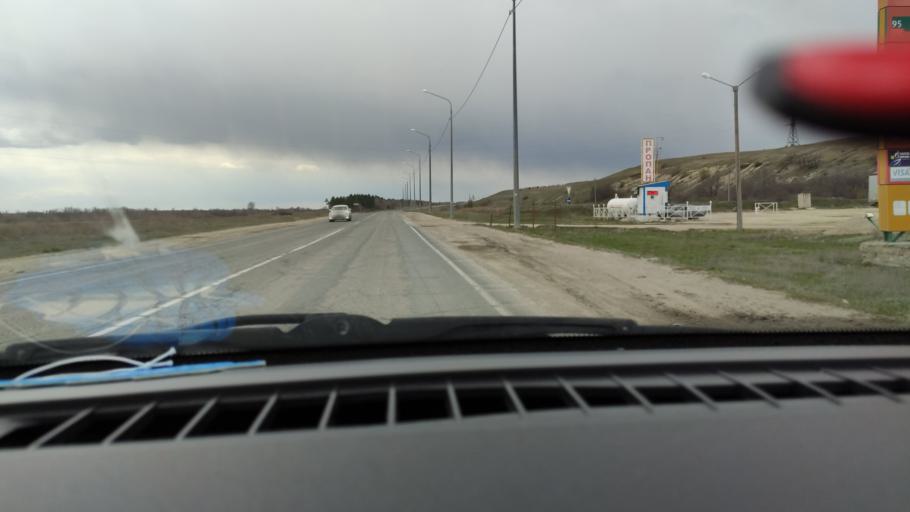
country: RU
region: Saratov
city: Sinodskoye
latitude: 52.0787
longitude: 46.7922
